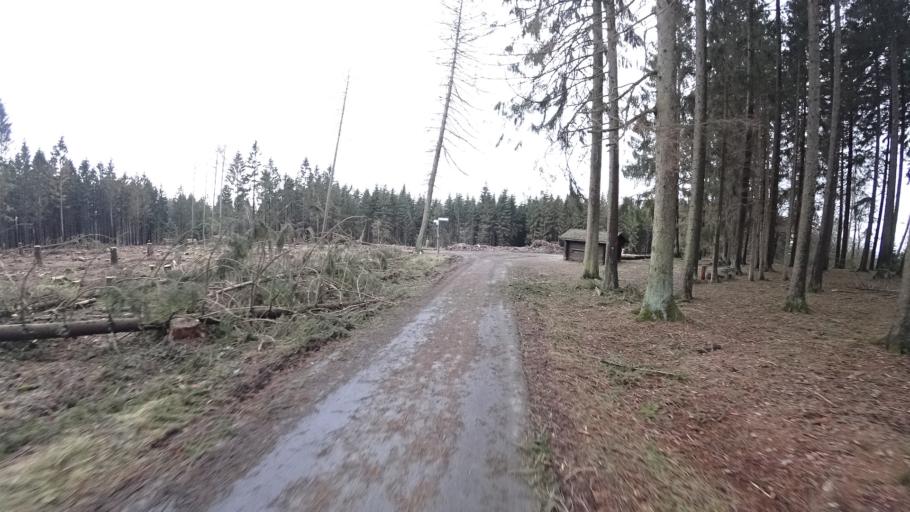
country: DE
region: Rheinland-Pfalz
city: Hillscheid
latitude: 50.4232
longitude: 7.7227
